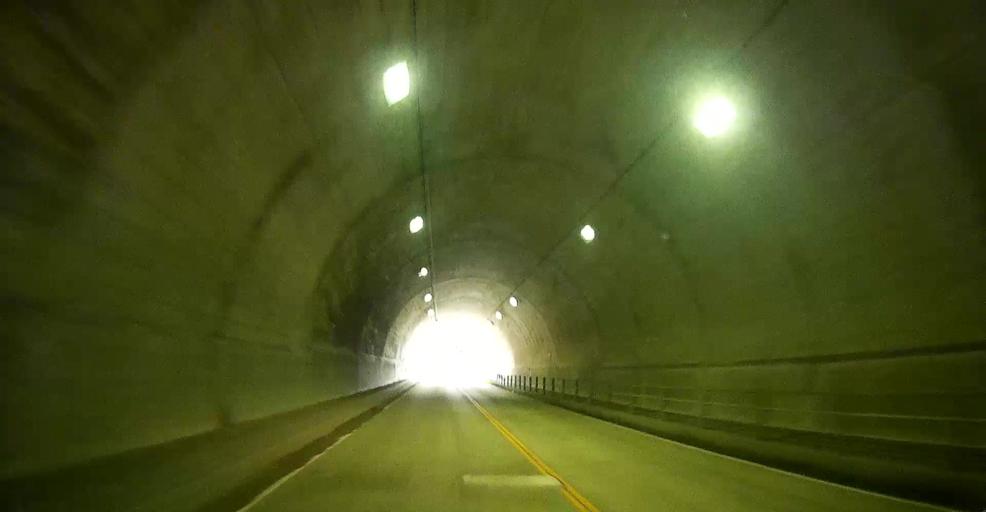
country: JP
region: Kumamoto
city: Matsubase
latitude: 32.6184
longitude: 130.8553
